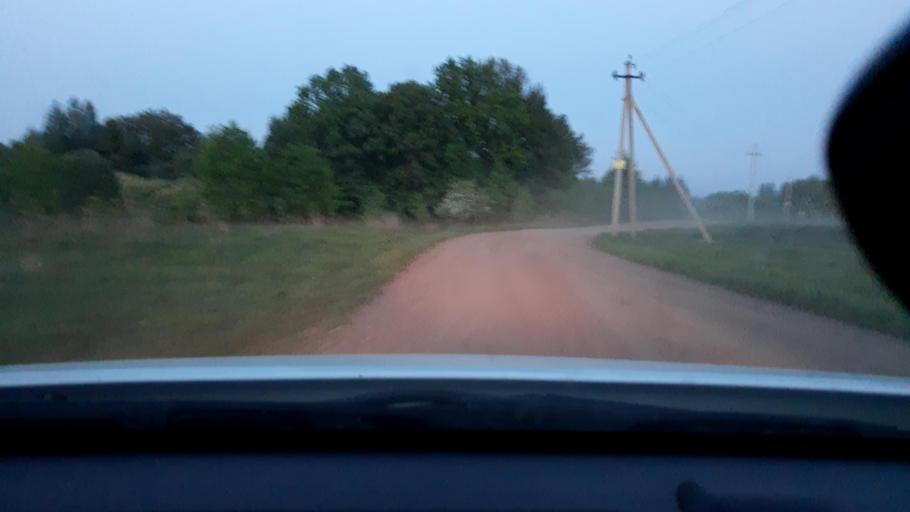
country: RU
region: Bashkortostan
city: Avdon
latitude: 54.5259
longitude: 55.8247
